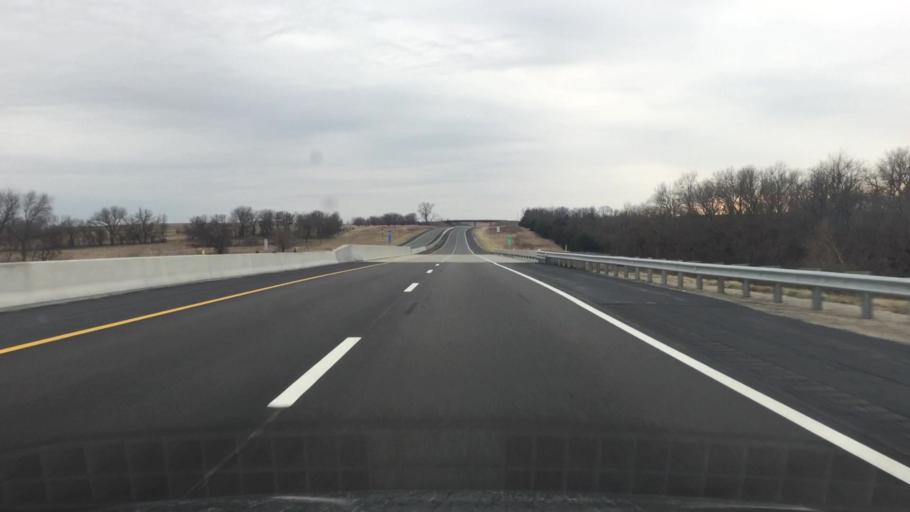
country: US
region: Kansas
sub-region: Osage County
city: Osage City
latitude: 38.7722
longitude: -95.9240
